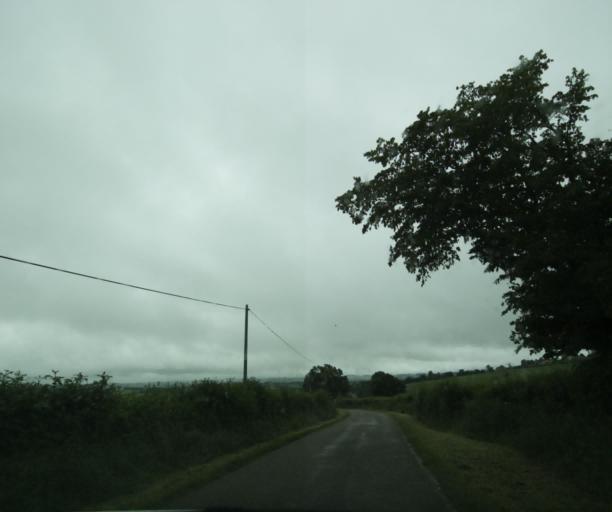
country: FR
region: Bourgogne
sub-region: Departement de Saone-et-Loire
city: Charolles
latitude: 46.3548
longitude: 4.2302
